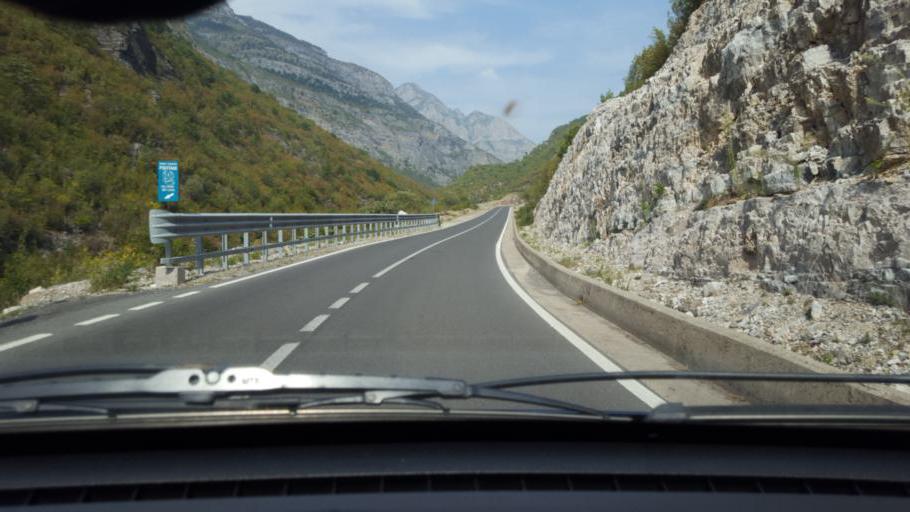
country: AL
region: Shkoder
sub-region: Rrethi i Malesia e Madhe
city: Kastrat
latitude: 42.4316
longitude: 19.5338
